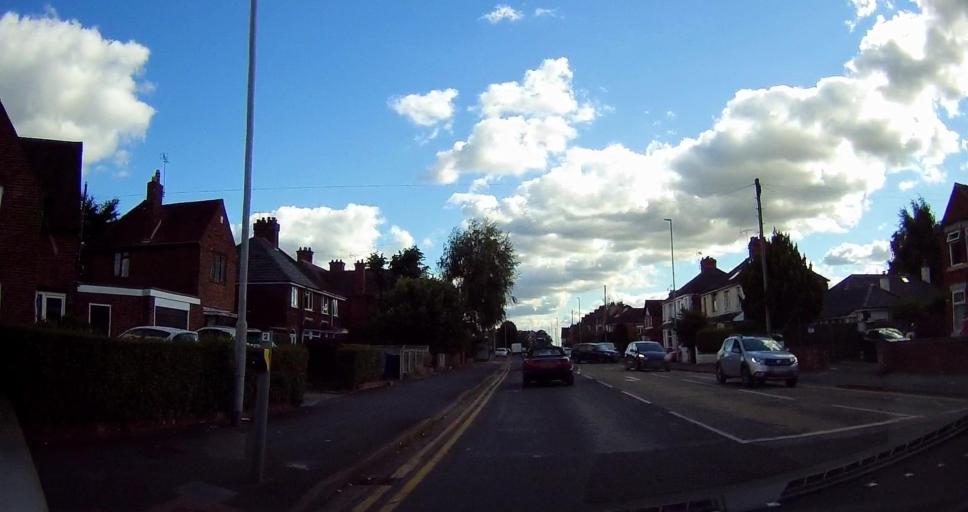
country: GB
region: England
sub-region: Staffordshire
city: Stafford
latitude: 52.8236
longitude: -2.1280
